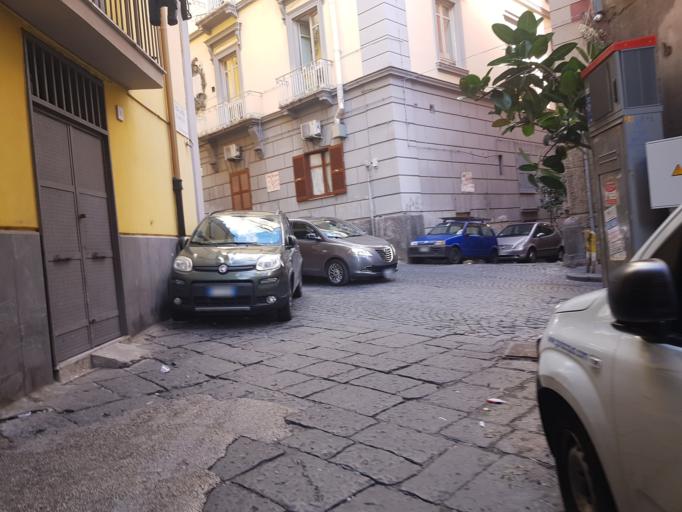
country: IT
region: Campania
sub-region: Provincia di Napoli
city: Napoli
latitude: 40.8429
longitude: 14.2474
